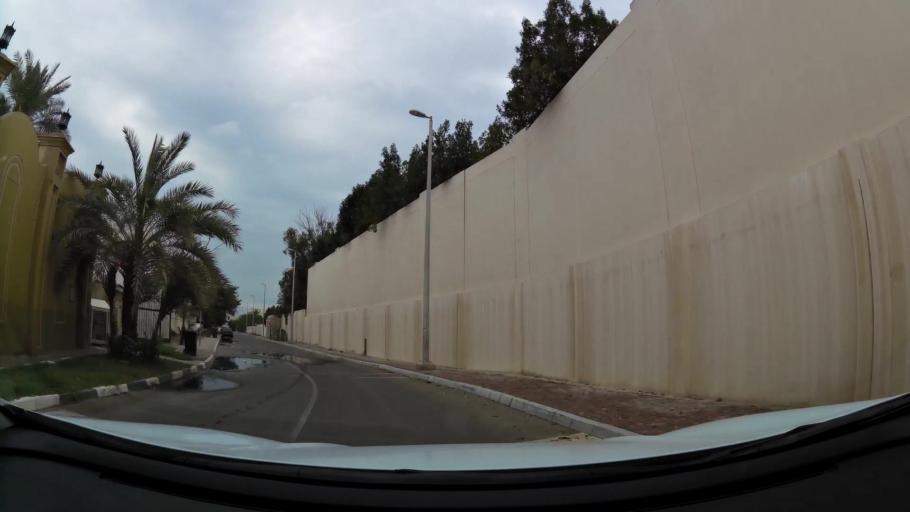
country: AE
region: Abu Dhabi
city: Abu Dhabi
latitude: 24.4366
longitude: 54.3845
